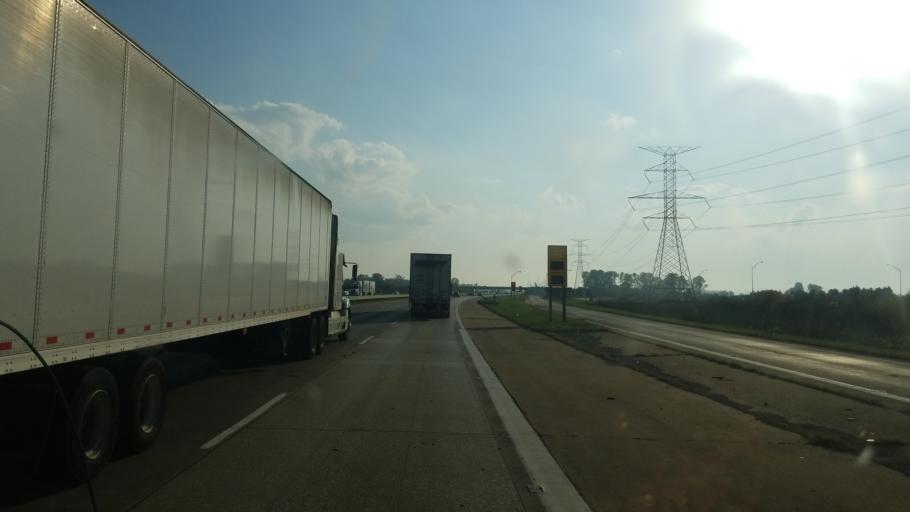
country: US
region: Michigan
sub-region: Monroe County
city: Luna Pier
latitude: 41.8293
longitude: -83.4301
